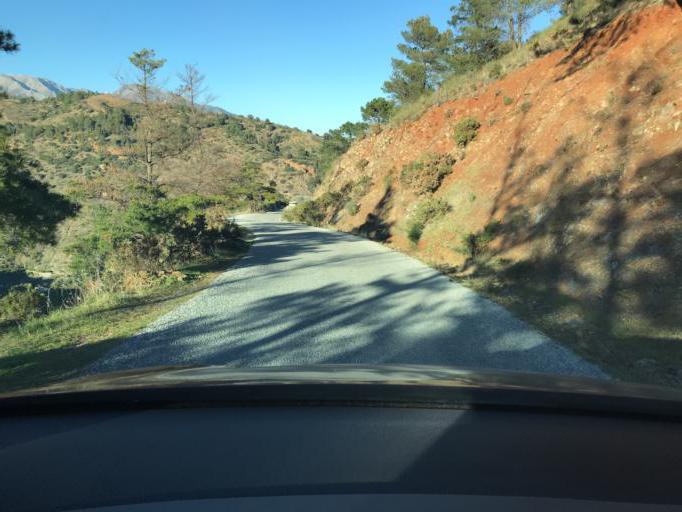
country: ES
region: Andalusia
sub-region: Provincia de Malaga
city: Tolox
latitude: 36.6847
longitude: -4.9127
